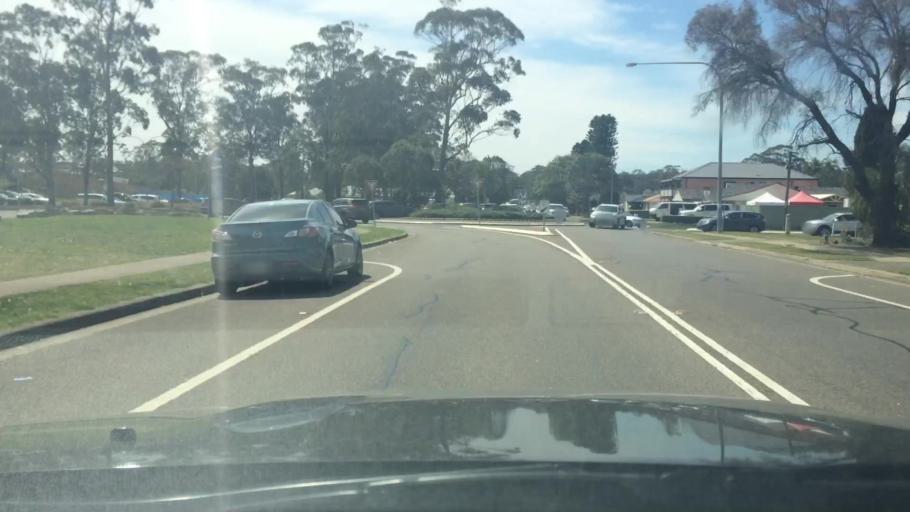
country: AU
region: New South Wales
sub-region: Fairfield
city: Cabramatta West
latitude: -33.8643
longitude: 150.8981
